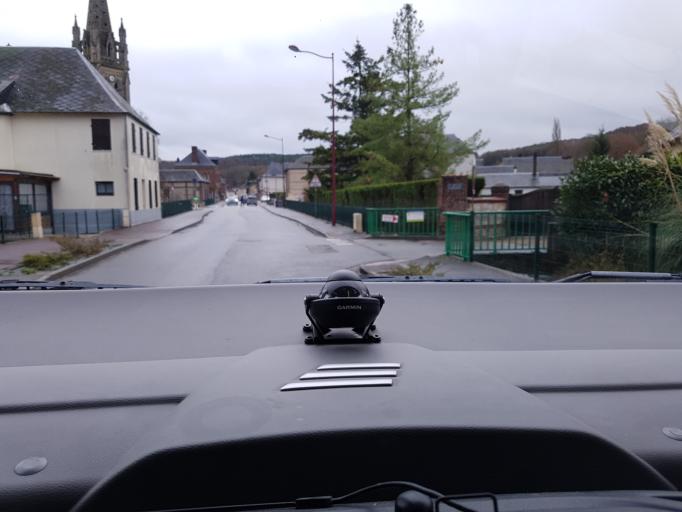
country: FR
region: Haute-Normandie
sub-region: Departement de l'Eure
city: Pont-Saint-Pierre
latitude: 49.3344
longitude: 1.2734
